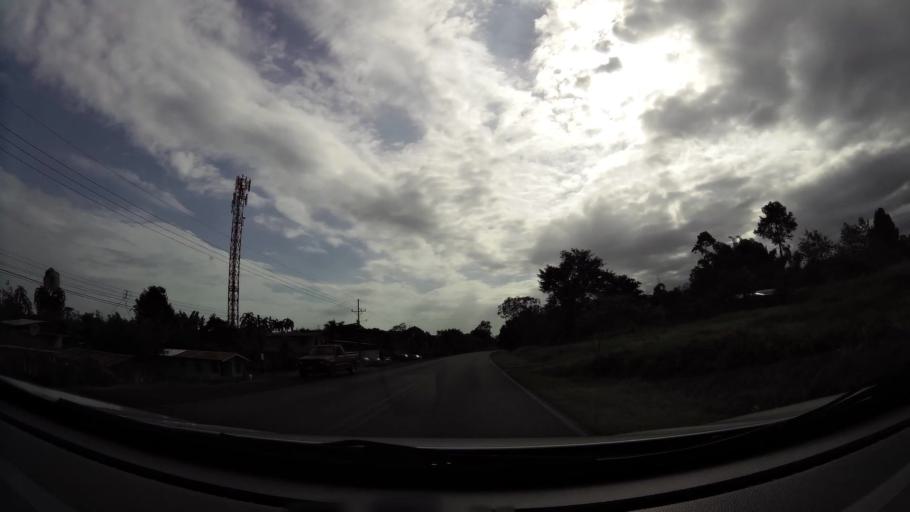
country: CR
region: Limon
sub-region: Canton de Guacimo
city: Guacimo
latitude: 10.1959
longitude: -83.6474
